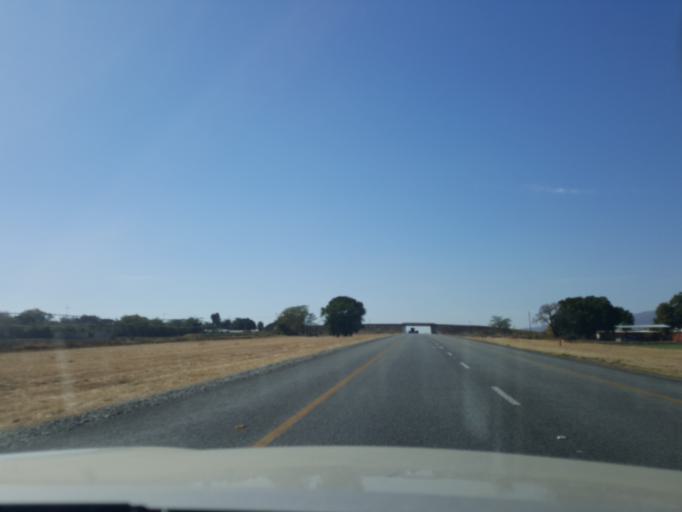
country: ZA
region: North-West
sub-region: Bojanala Platinum District Municipality
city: Brits
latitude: -25.6800
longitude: 27.8139
